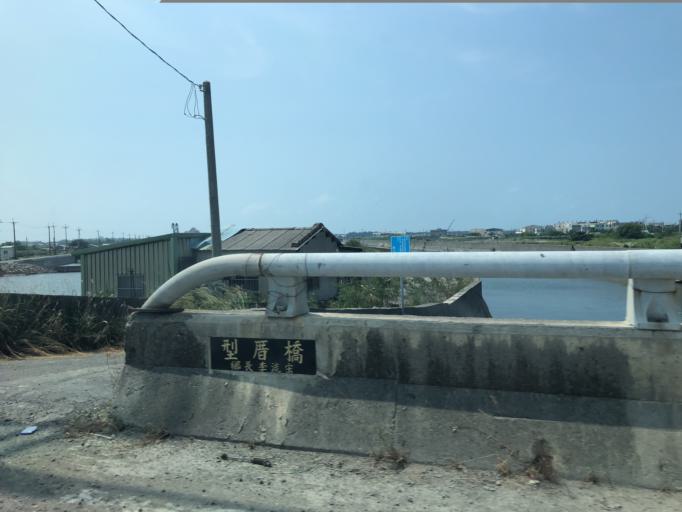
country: TW
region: Taiwan
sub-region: Chiayi
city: Taibao
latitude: 23.4712
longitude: 120.1529
